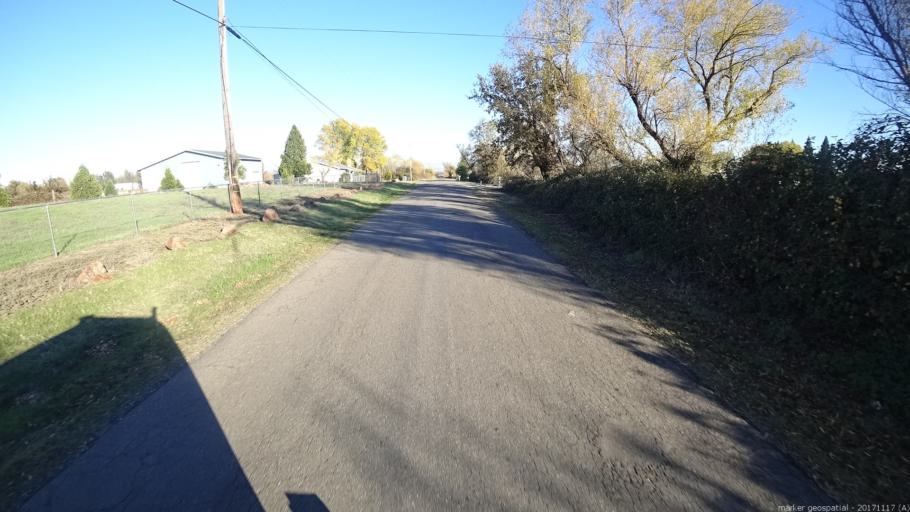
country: US
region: California
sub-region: Shasta County
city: Cottonwood
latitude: 40.4161
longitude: -122.2424
